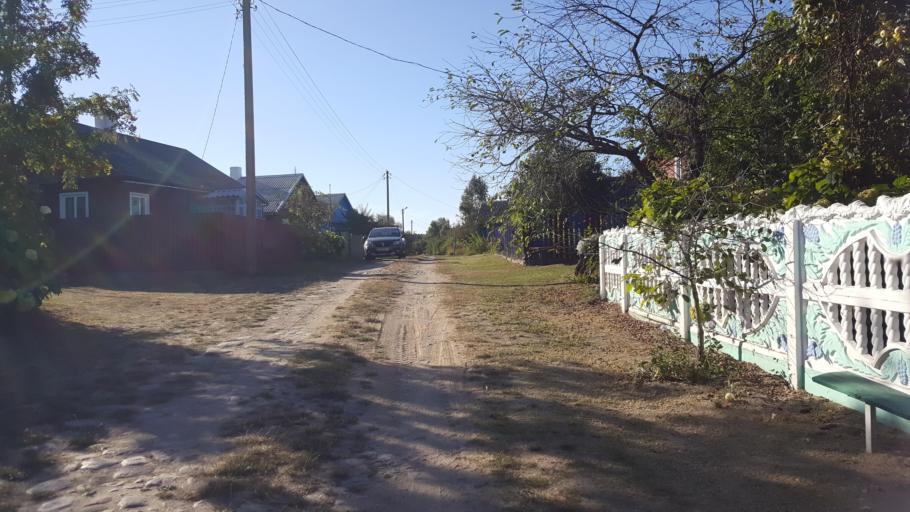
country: BY
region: Brest
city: Vysokaye
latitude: 52.3266
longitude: 23.2503
